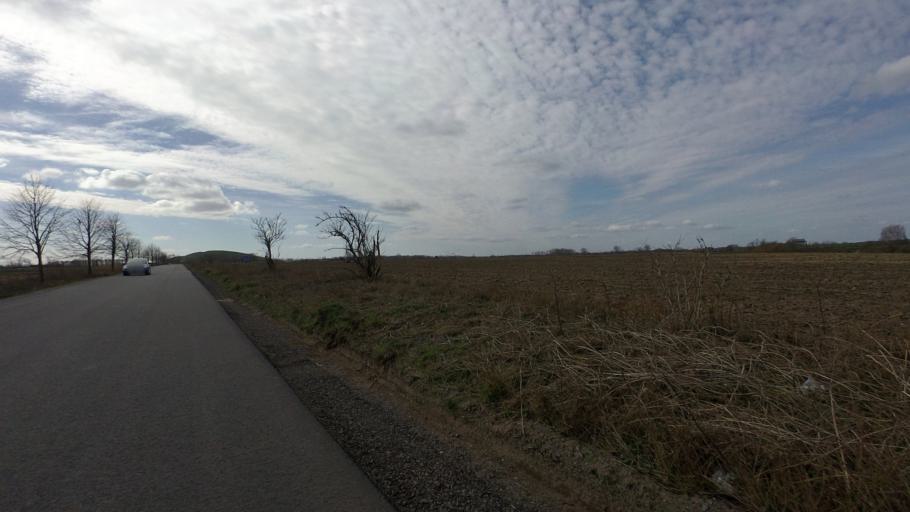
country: DE
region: Berlin
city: Blankenfelde
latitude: 52.6534
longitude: 13.4213
